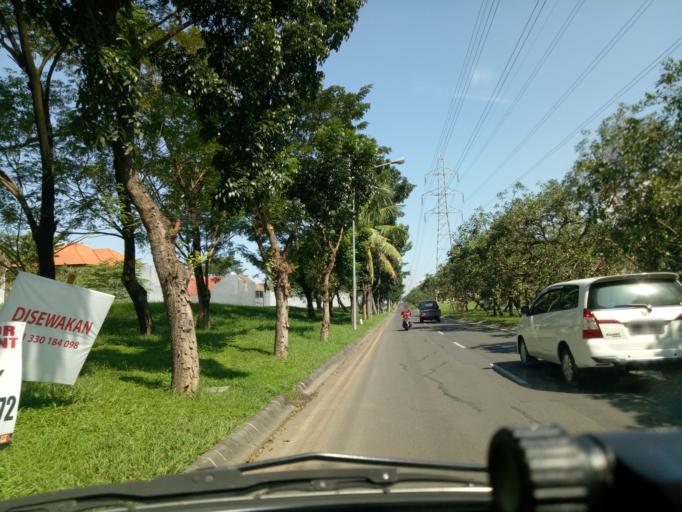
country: ID
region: East Java
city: Driyorejo
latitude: -7.2847
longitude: 112.6471
